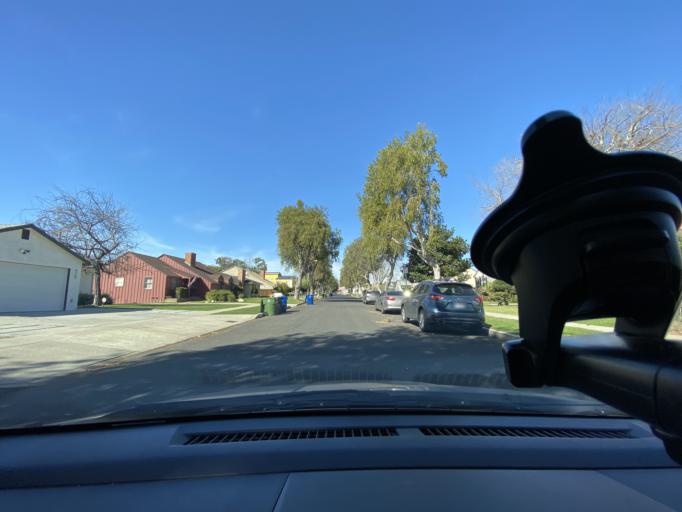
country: US
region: California
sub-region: Los Angeles County
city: Westwood, Los Angeles
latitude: 34.0236
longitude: -118.4307
